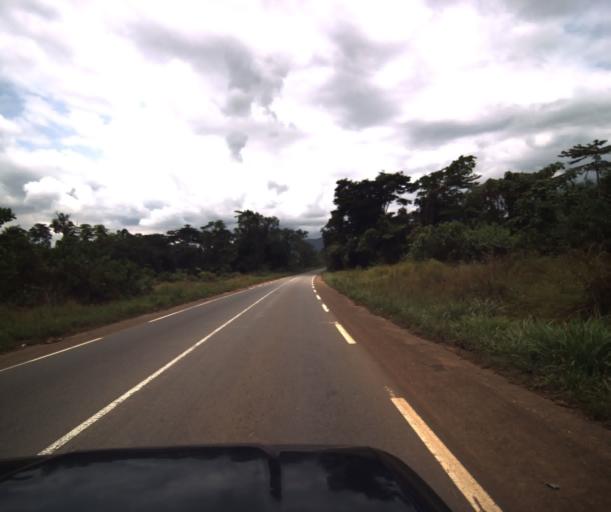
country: CM
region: Centre
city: Eseka
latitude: 3.8766
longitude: 10.8159
